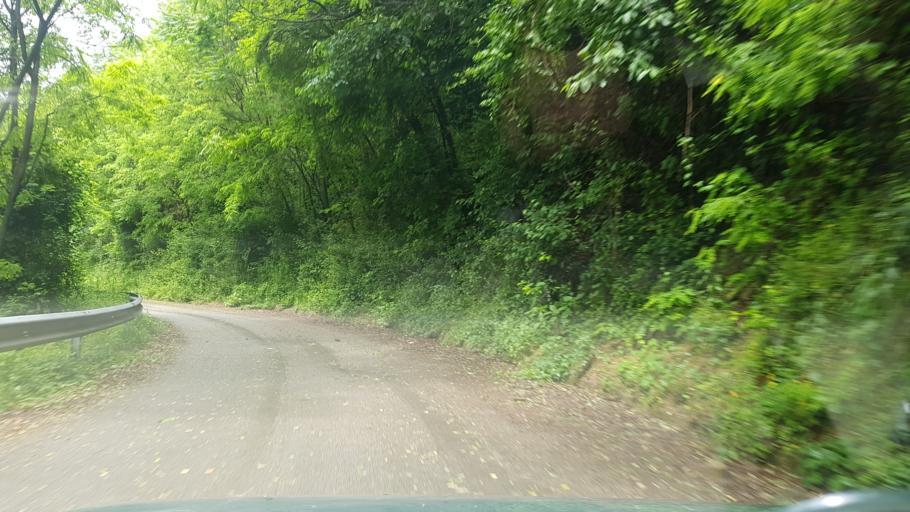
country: IT
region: Friuli Venezia Giulia
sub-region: Provincia di Gorizia
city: Gorizia
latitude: 45.9473
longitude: 13.5907
